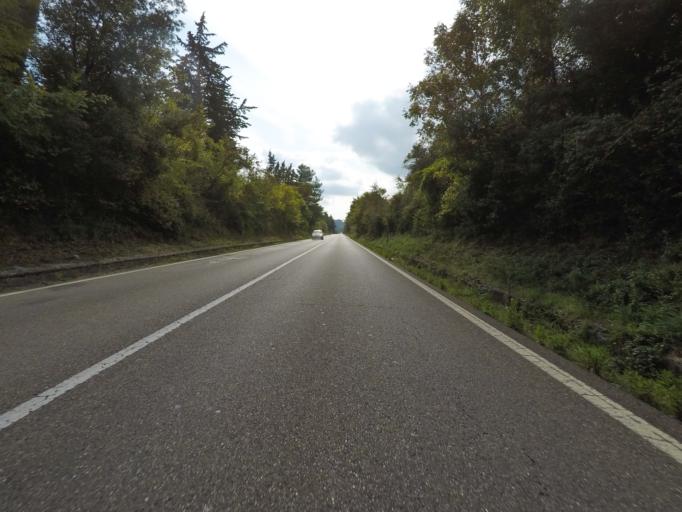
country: IT
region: Tuscany
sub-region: Provincia di Siena
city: Murlo
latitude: 43.1266
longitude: 11.2960
